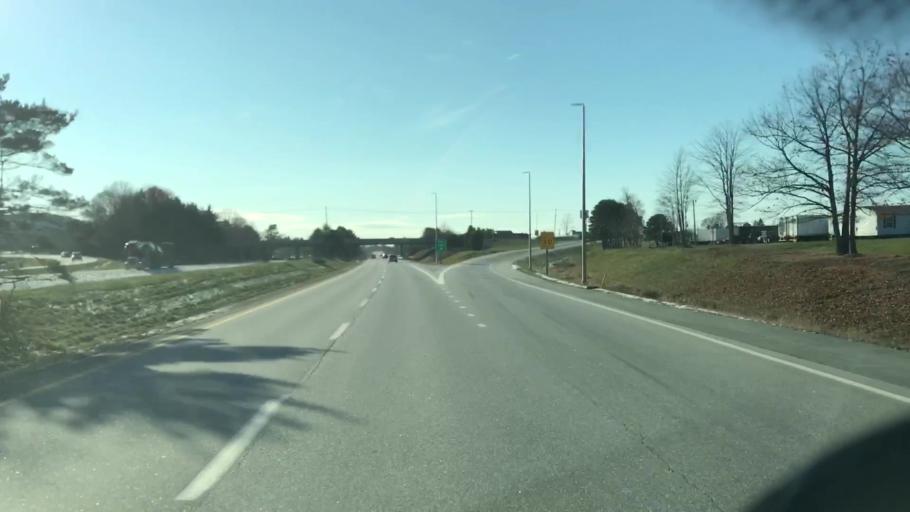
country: US
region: Maine
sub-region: Penobscot County
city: Hampden
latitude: 44.7751
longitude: -68.8555
